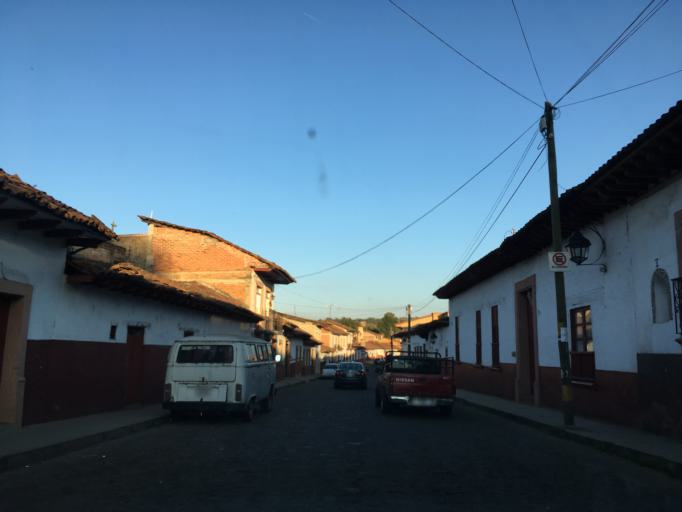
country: MX
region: Michoacan
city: Patzcuaro
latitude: 19.5134
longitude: -101.6158
